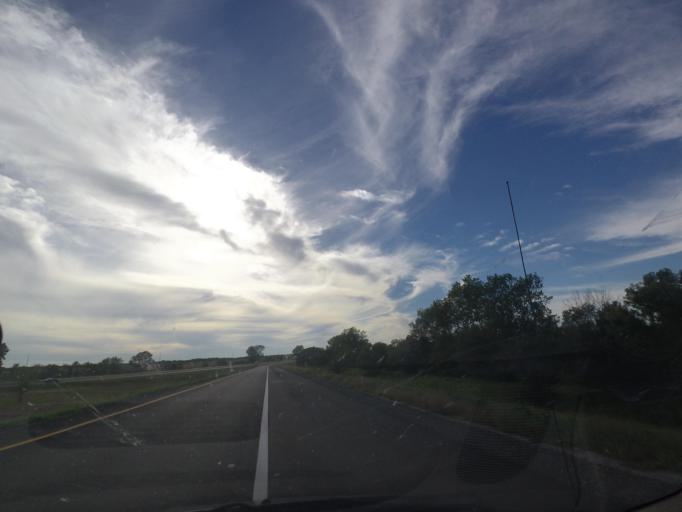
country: US
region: Illinois
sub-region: Macon County
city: Harristown
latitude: 39.8362
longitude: -89.1575
